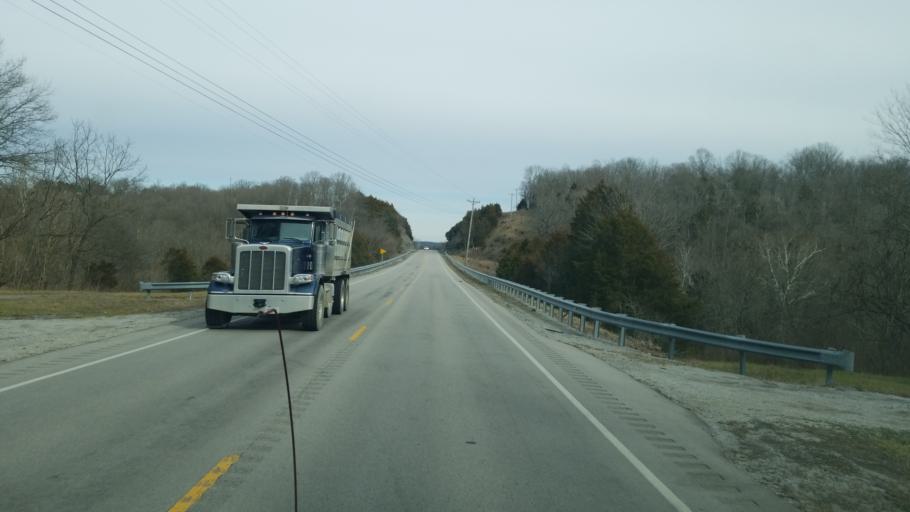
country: US
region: Kentucky
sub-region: Nicholas County
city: Carlisle
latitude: 38.4119
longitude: -84.0081
